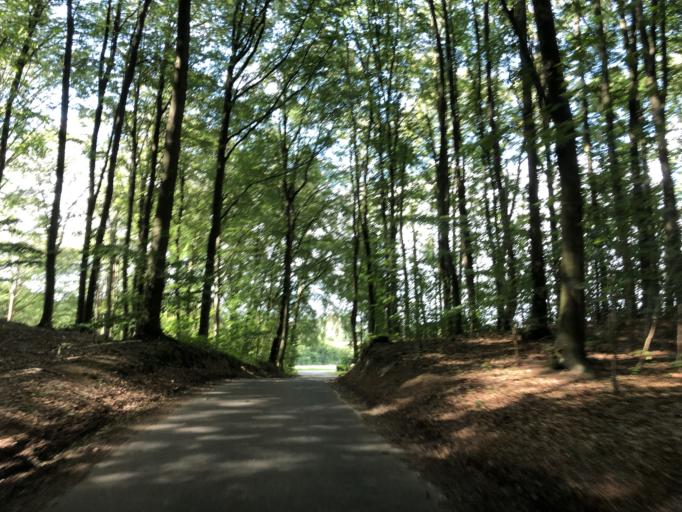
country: DK
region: South Denmark
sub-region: Vejle Kommune
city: Brejning
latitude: 55.6866
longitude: 9.6692
